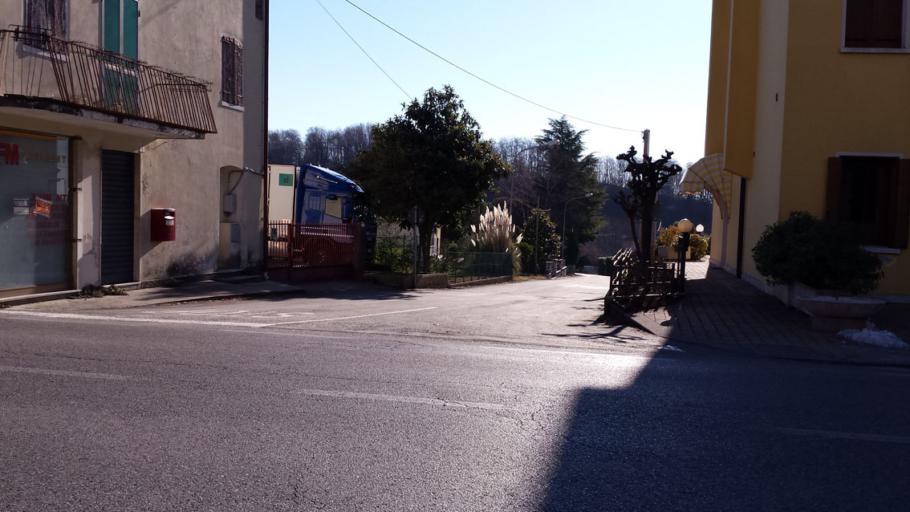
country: IT
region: Veneto
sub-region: Provincia di Treviso
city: Paderno del Grappa
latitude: 45.8367
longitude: 11.8545
